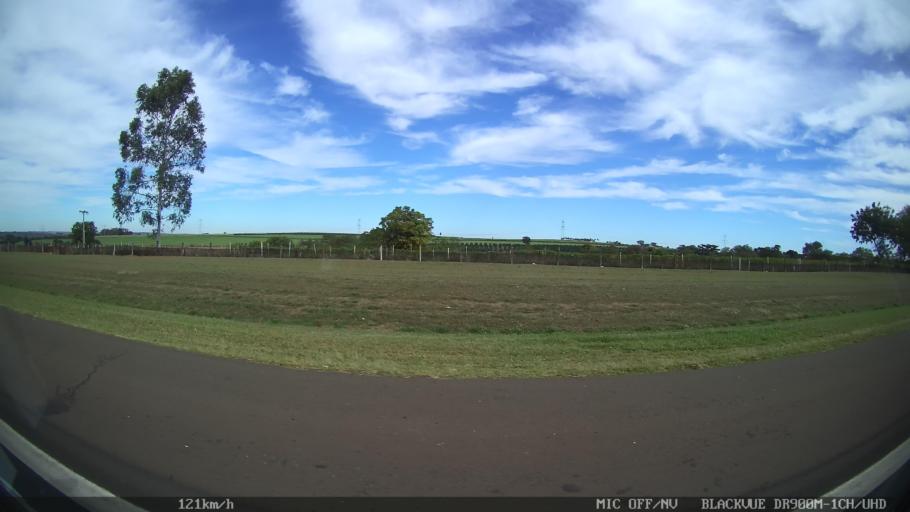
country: BR
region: Sao Paulo
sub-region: Santa Adelia
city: Santa Adelia
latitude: -21.3670
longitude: -48.7555
